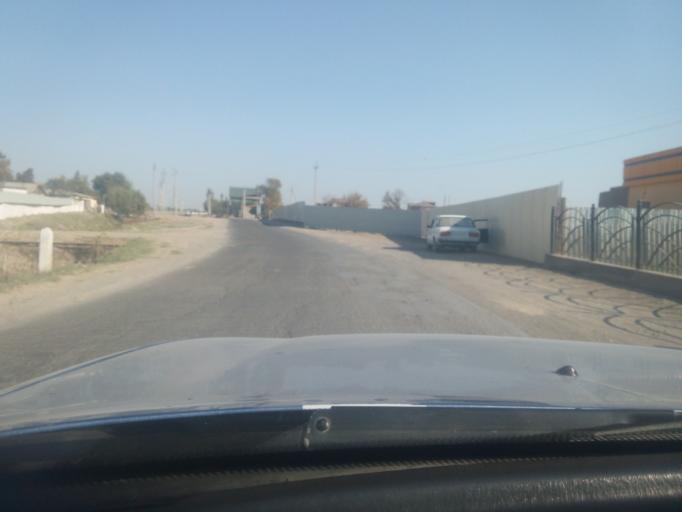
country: UZ
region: Sirdaryo
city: Guliston
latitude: 40.4947
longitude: 68.8005
